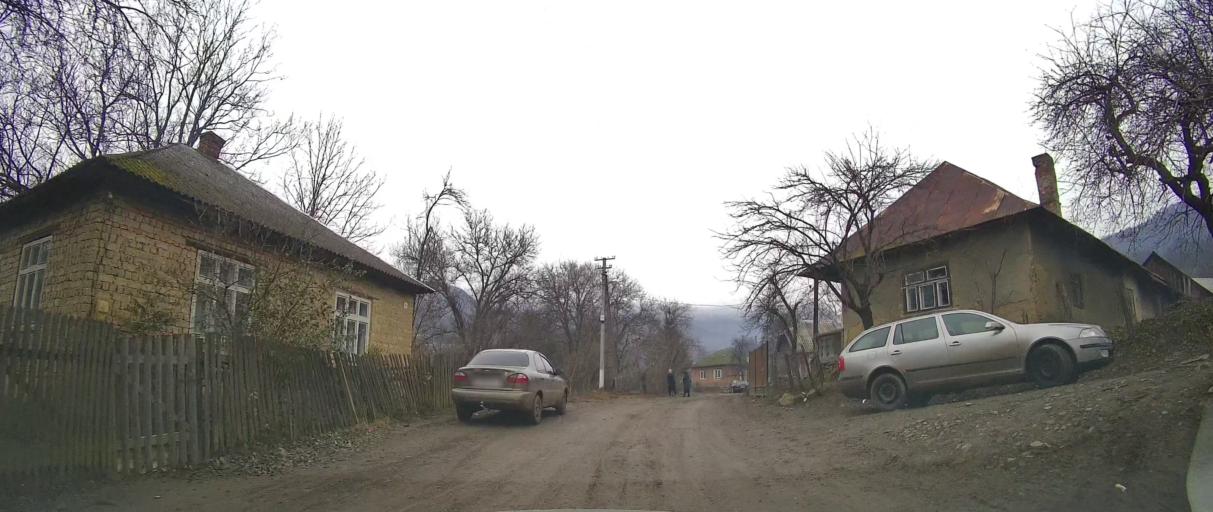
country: UA
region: Zakarpattia
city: Velykyi Bereznyi
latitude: 48.9693
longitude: 22.5503
